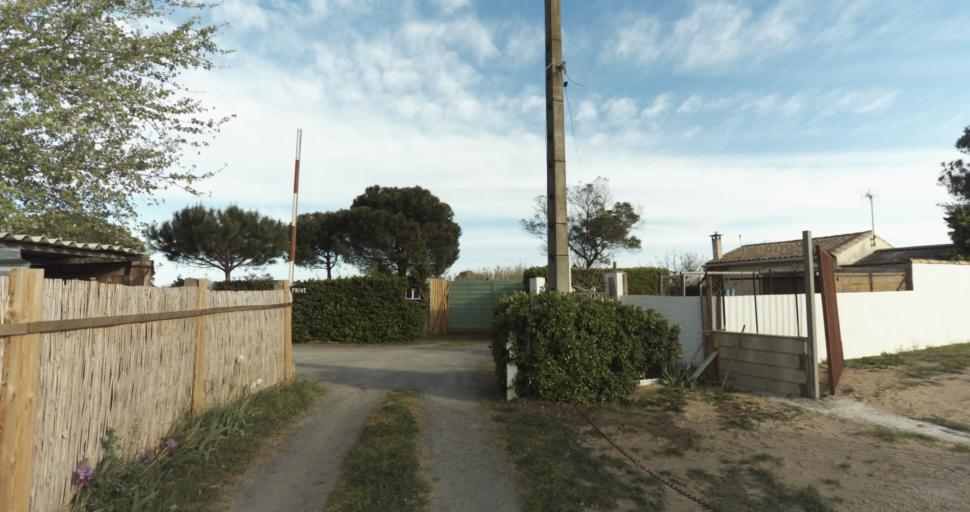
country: FR
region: Languedoc-Roussillon
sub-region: Departement de l'Herault
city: Marseillan
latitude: 43.3182
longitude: 3.5392
